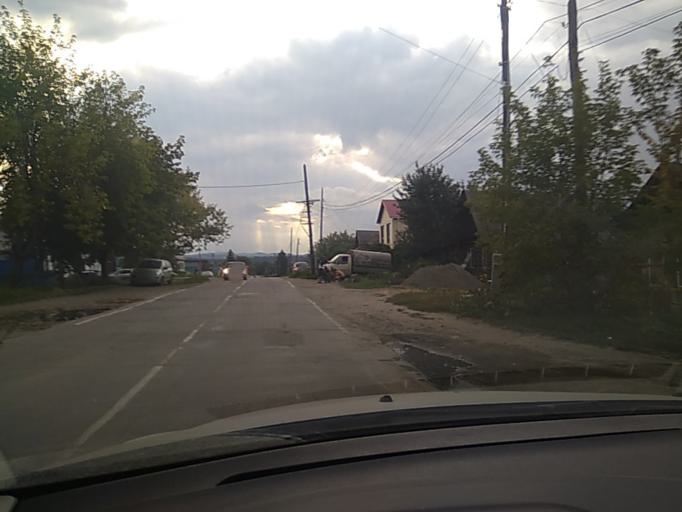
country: RU
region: Chelyabinsk
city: Kyshtym
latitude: 55.6971
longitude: 60.5517
